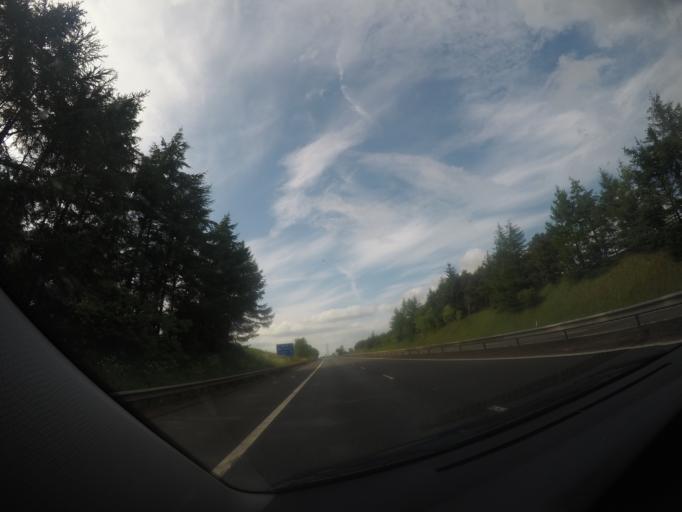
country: GB
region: Scotland
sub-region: South Lanarkshire
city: Douglas
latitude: 55.6019
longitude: -3.8379
